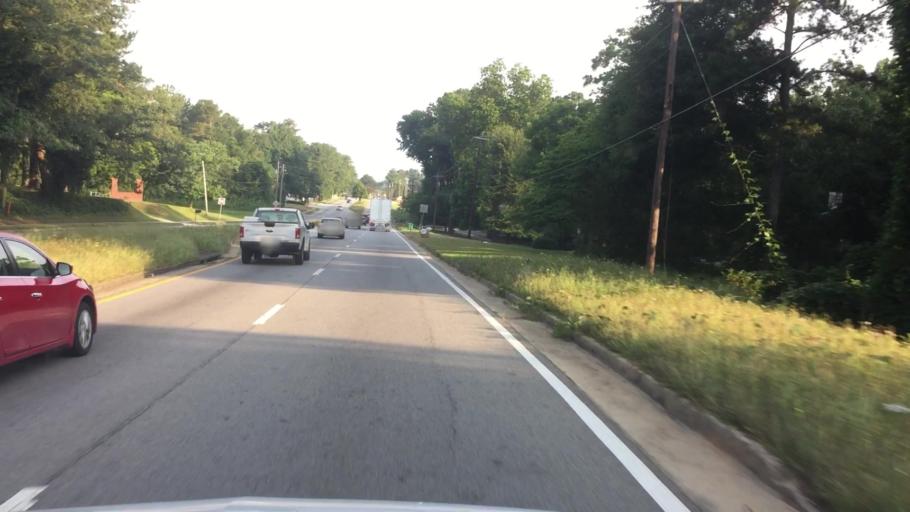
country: US
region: Georgia
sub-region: DeKalb County
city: Panthersville
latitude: 33.6867
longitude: -84.2520
